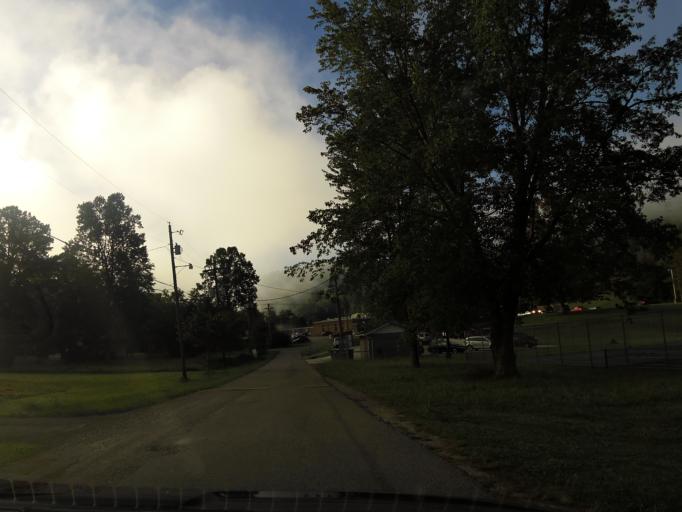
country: US
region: Tennessee
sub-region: Campbell County
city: Jellico
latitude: 36.5772
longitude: -84.1296
